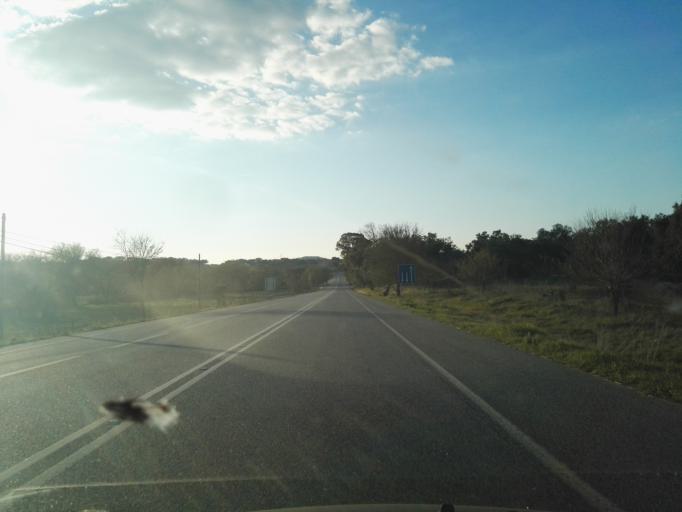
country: PT
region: Evora
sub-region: Arraiolos
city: Arraiolos
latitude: 38.6123
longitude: -8.0697
